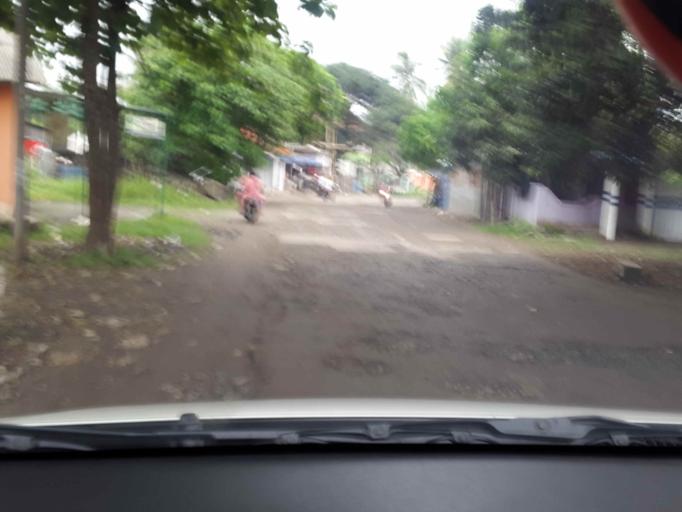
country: ID
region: West Java
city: Cidadap
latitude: -7.0141
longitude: 106.5434
